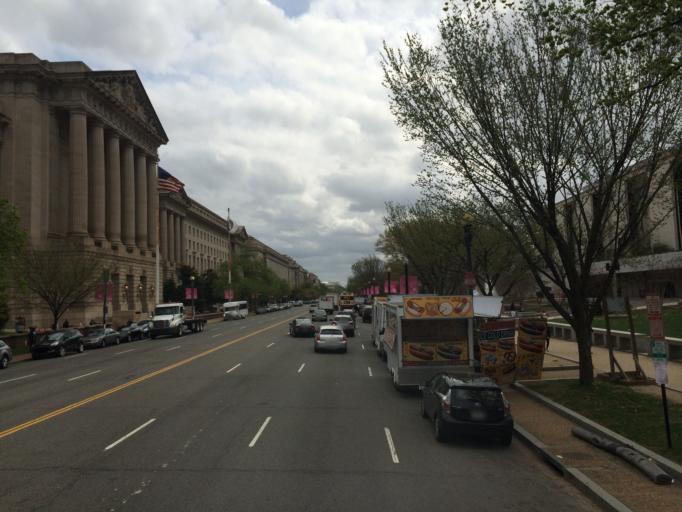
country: US
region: Washington, D.C.
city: Washington, D.C.
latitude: 38.8920
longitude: -77.0312
